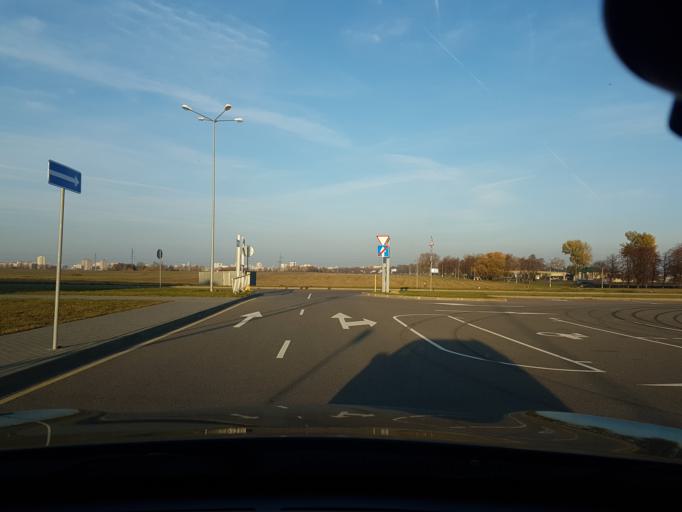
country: BY
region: Minsk
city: Shchomyslitsa
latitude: 53.8235
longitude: 27.4396
